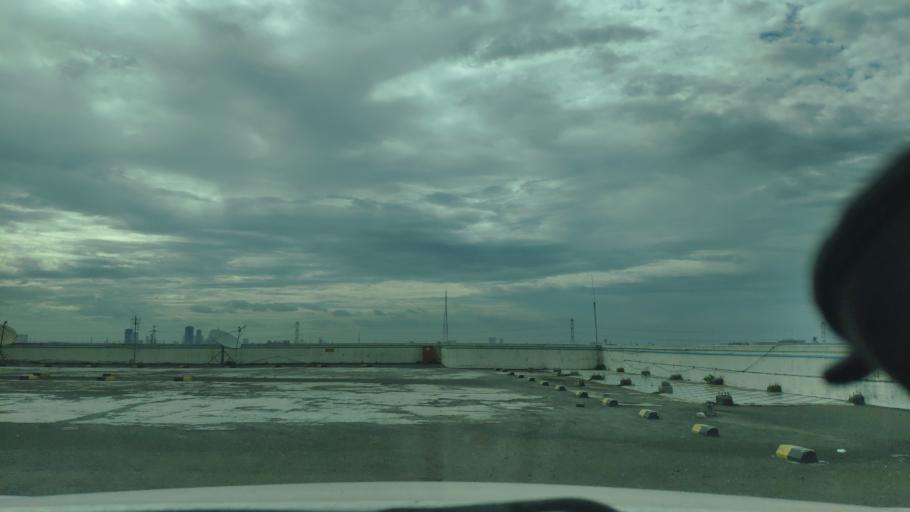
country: ID
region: West Java
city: Ciputat
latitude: -6.2232
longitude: 106.7083
